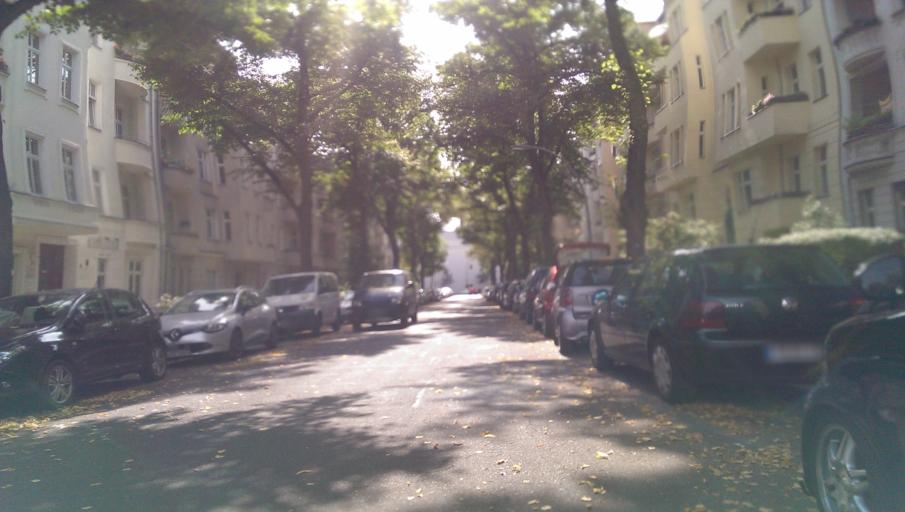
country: DE
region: Berlin
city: Tempelhof Bezirk
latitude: 52.4579
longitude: 13.3871
